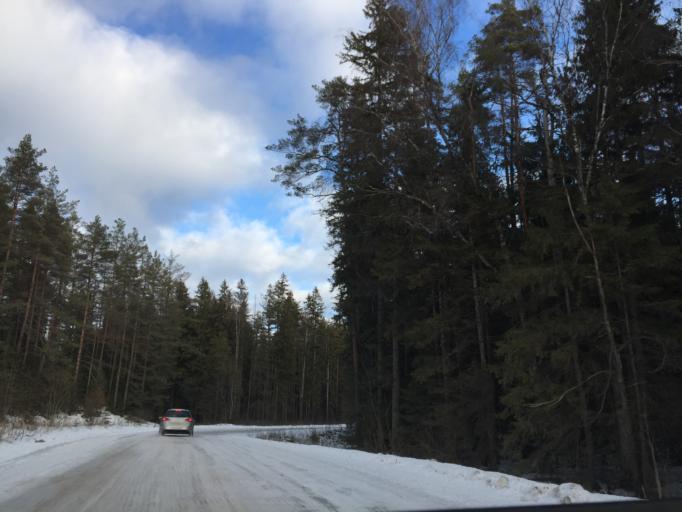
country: LV
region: Ogre
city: Jumprava
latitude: 56.5807
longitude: 24.9522
